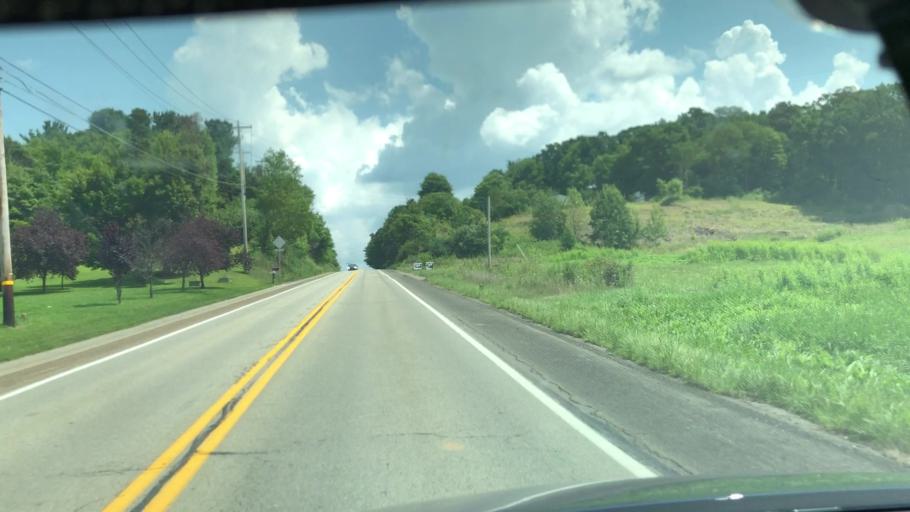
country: US
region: Pennsylvania
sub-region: Armstrong County
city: Freeport
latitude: 40.7094
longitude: -79.7324
